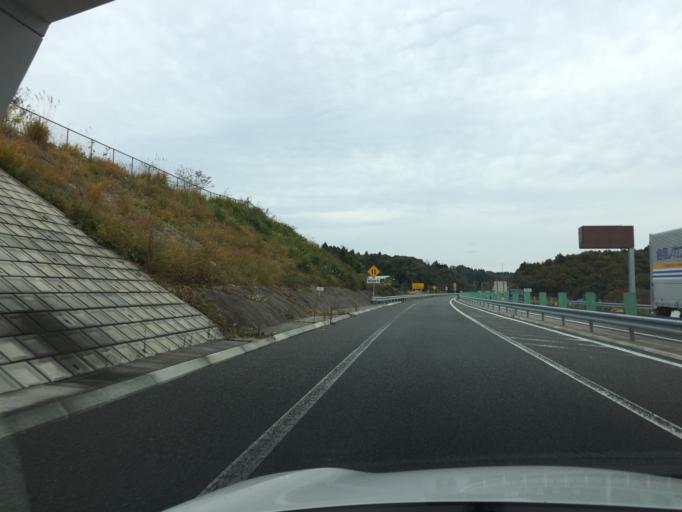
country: JP
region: Fukushima
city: Ishikawa
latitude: 37.2033
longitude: 140.4481
